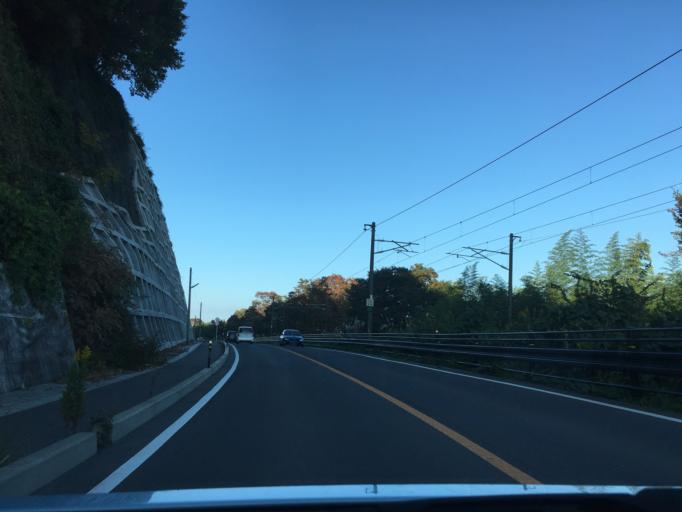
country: JP
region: Fukushima
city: Sukagawa
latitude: 37.3106
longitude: 140.3771
